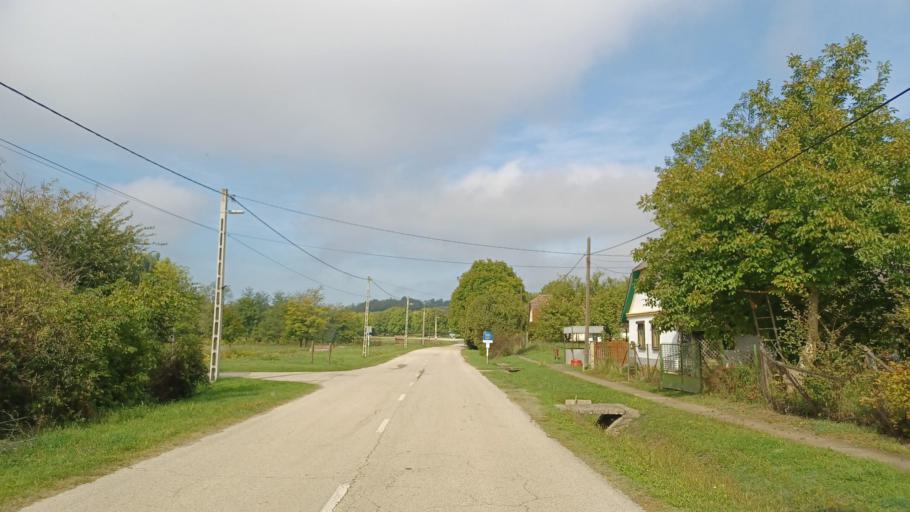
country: HU
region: Tolna
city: Pincehely
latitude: 46.6490
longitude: 18.5193
